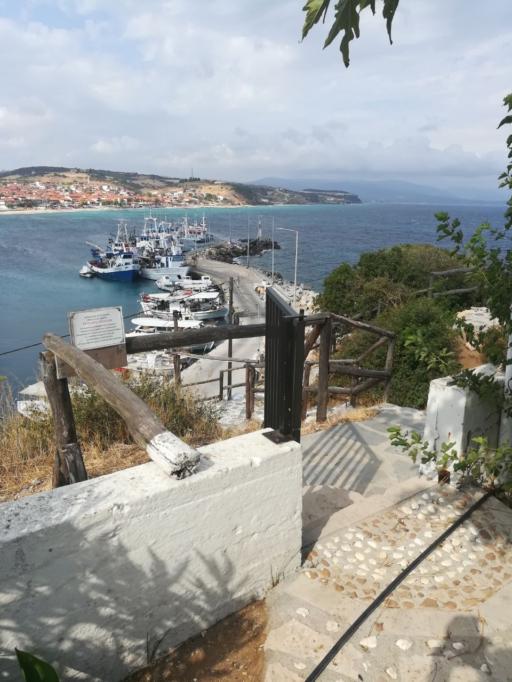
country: GR
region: Central Macedonia
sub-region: Nomos Chalkidikis
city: Nea Roda
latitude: 40.3822
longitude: 23.9341
